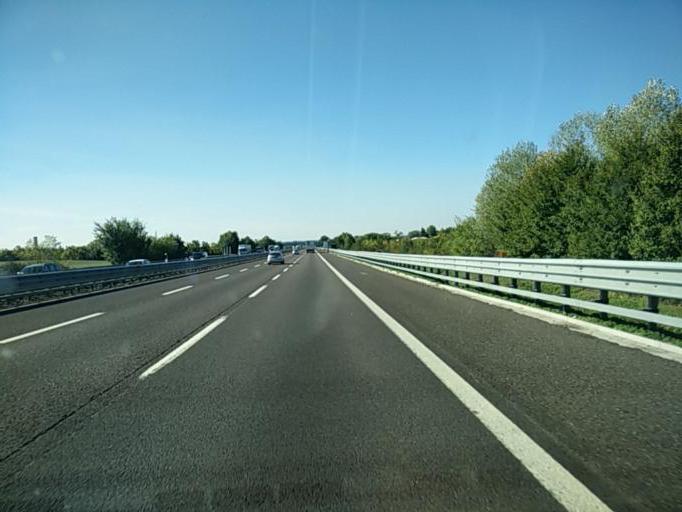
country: IT
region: Lombardy
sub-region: Provincia di Brescia
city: Pozzolengo
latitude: 45.4329
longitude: 10.6308
